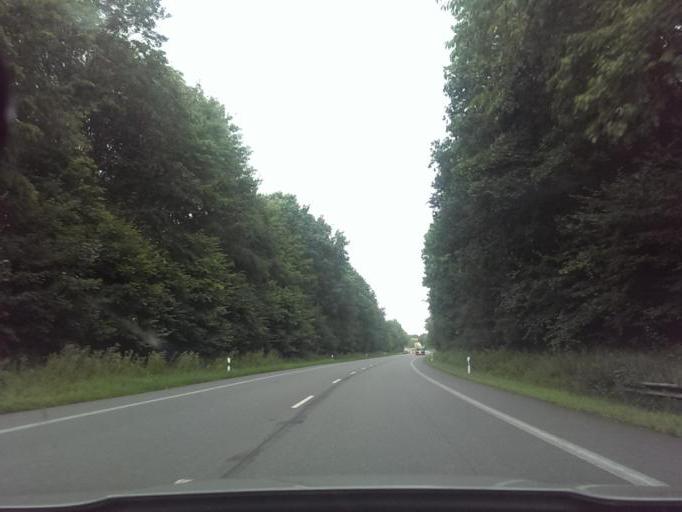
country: DE
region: North Rhine-Westphalia
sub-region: Regierungsbezirk Detmold
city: Steinheim
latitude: 51.8869
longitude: 9.0903
